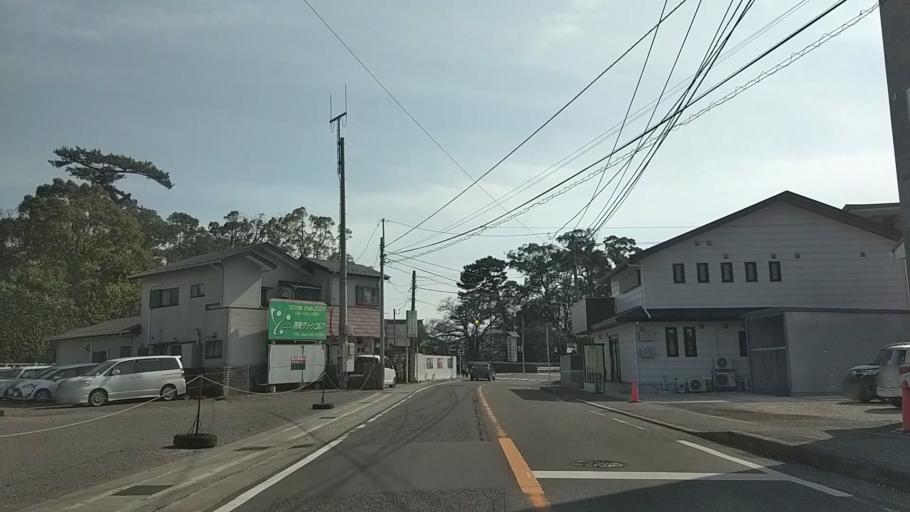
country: JP
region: Kanagawa
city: Chigasaki
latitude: 35.3789
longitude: 139.3808
